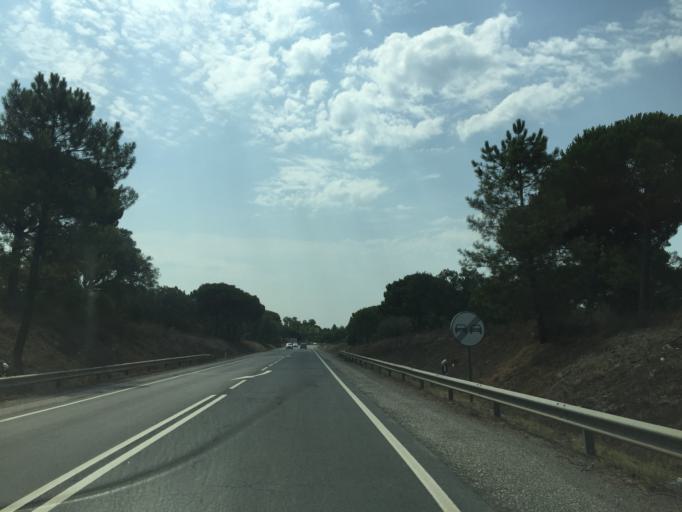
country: PT
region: Setubal
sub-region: Alcacer do Sal
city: Alcacer do Sal
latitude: 38.3508
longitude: -8.5201
